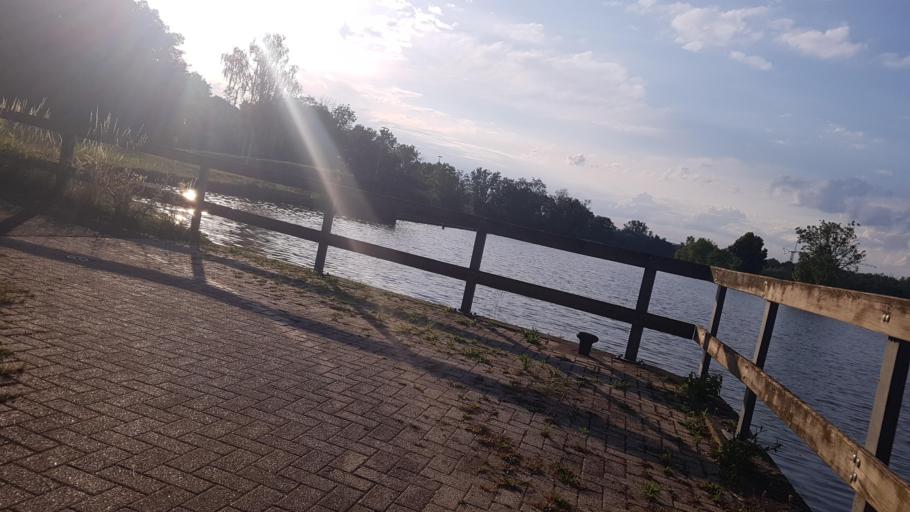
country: FR
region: Alsace
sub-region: Departement du Bas-Rhin
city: Dettwiller
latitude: 48.7501
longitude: 7.4529
